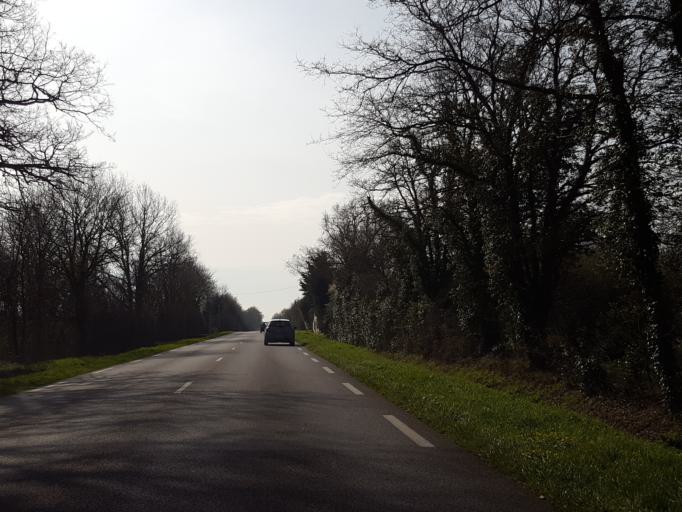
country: FR
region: Pays de la Loire
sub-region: Departement de la Vendee
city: Les Lucs-sur-Boulogne
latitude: 46.8267
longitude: -1.4767
